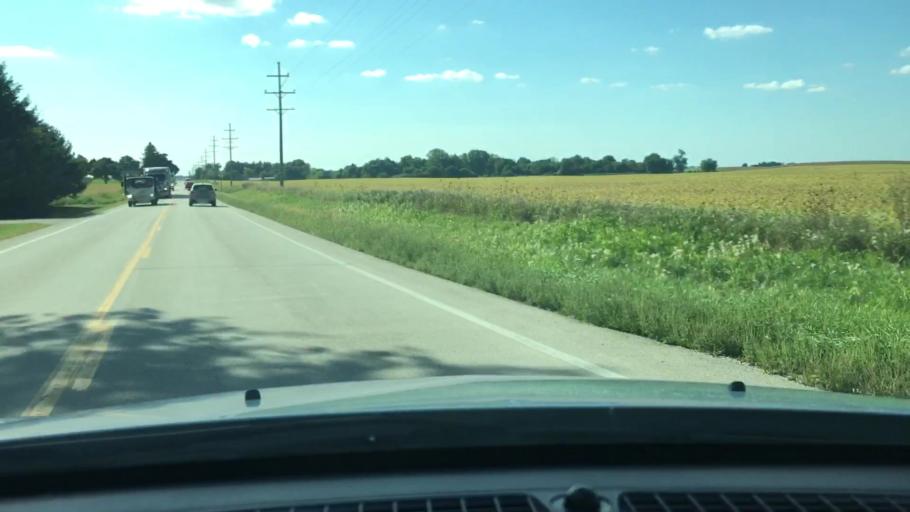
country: US
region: Illinois
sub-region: DeKalb County
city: Waterman
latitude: 41.8492
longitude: -88.7736
